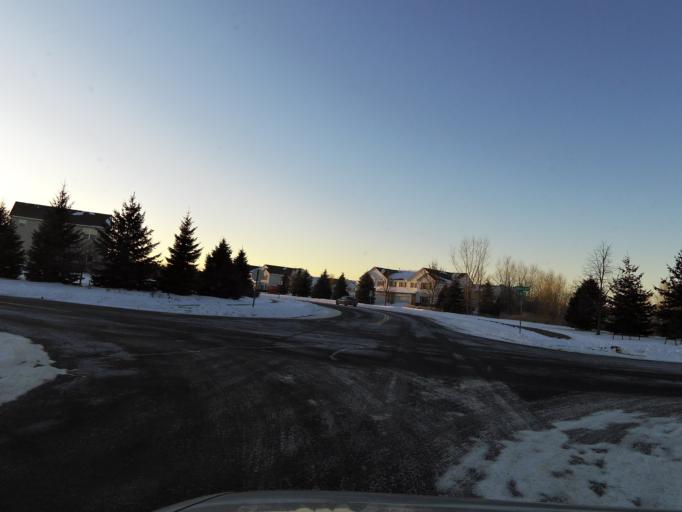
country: US
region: Minnesota
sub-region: Dakota County
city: Rosemount
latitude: 44.7425
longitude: -93.1006
